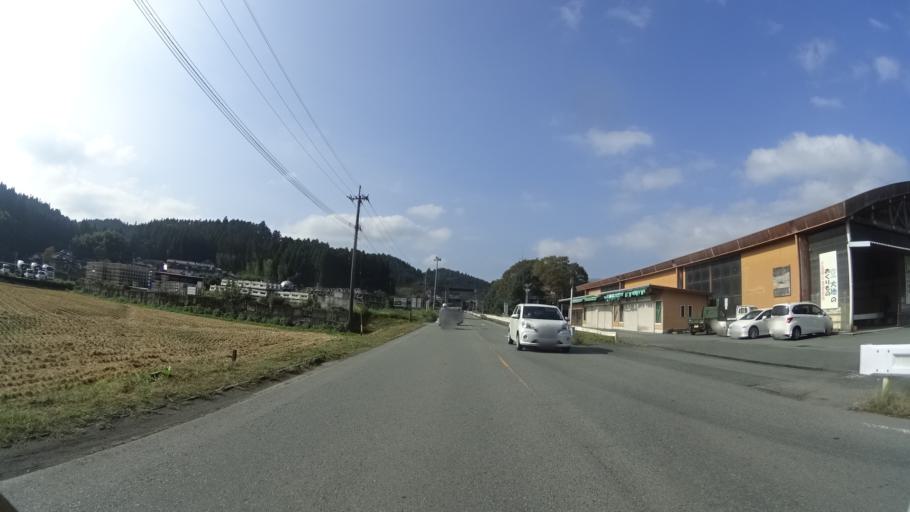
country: JP
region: Kumamoto
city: Aso
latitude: 33.1110
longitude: 131.0629
